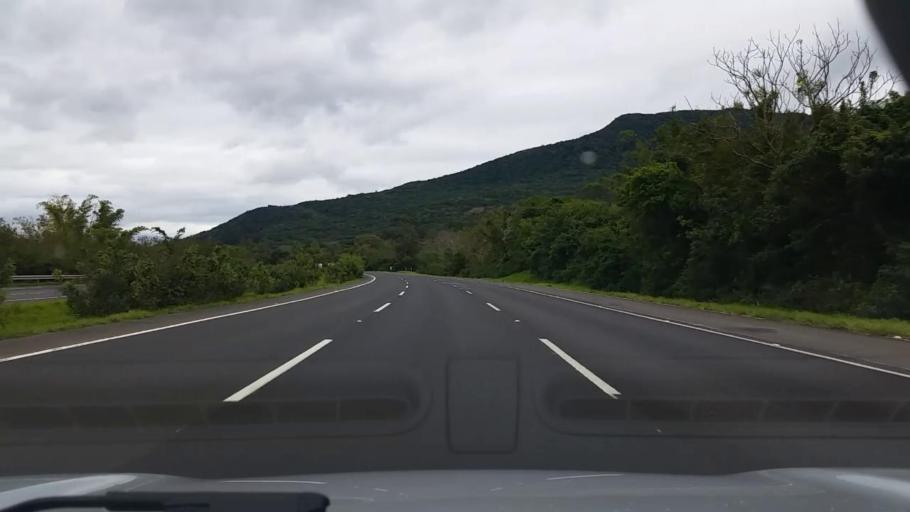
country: BR
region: Rio Grande do Sul
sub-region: Osorio
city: Osorio
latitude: -29.8931
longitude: -50.3536
